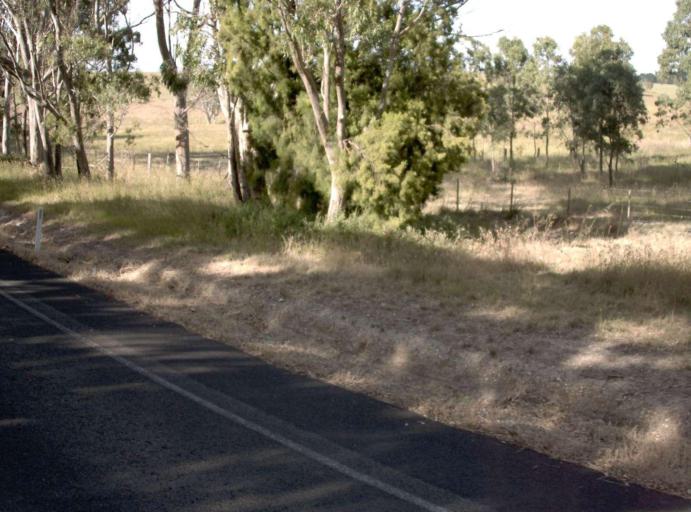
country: AU
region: Victoria
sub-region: East Gippsland
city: Lakes Entrance
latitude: -37.8631
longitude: 147.8475
